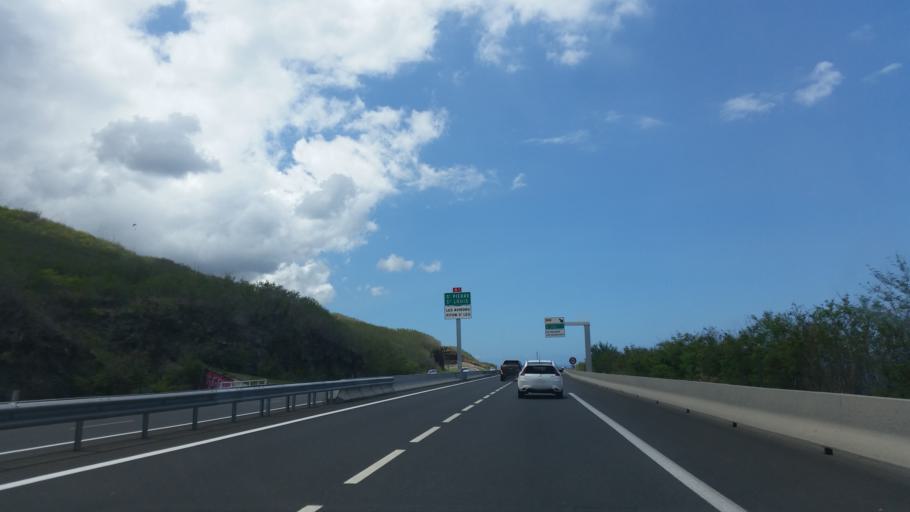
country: RE
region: Reunion
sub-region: Reunion
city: Saint-Leu
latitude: -21.1356
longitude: 55.2853
